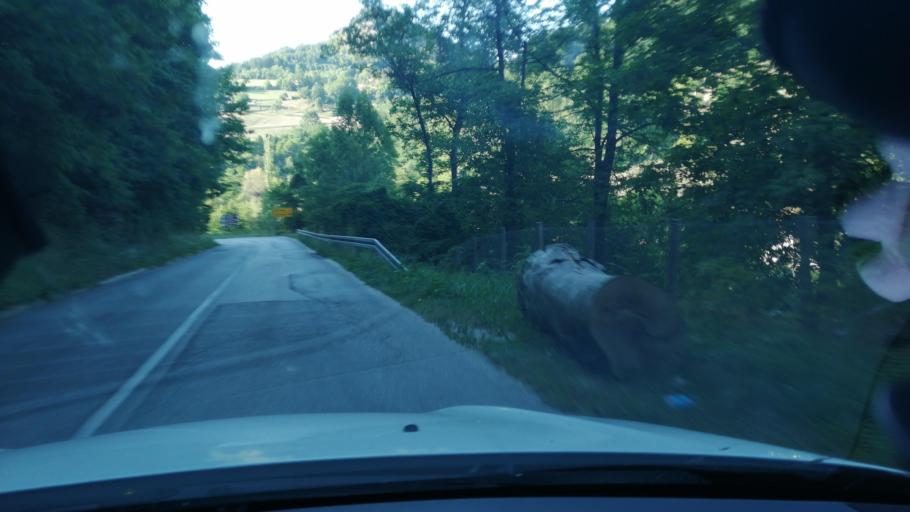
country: RS
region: Central Serbia
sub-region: Moravicki Okrug
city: Ivanjica
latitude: 43.6754
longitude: 20.2599
